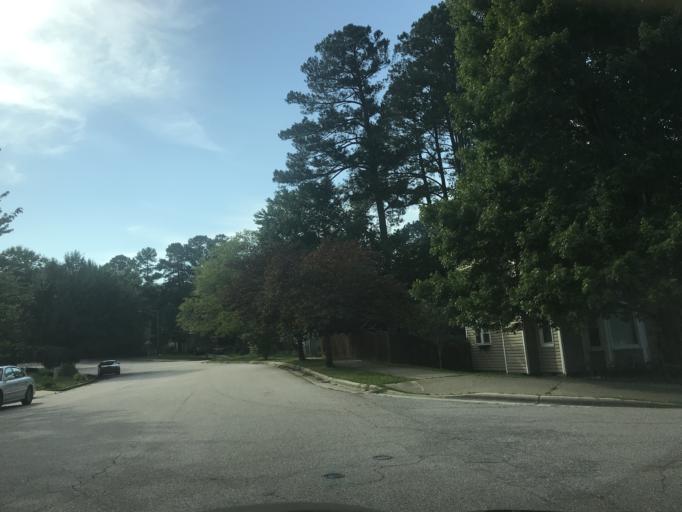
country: US
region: North Carolina
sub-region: Wake County
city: Raleigh
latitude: 35.8162
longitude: -78.5653
